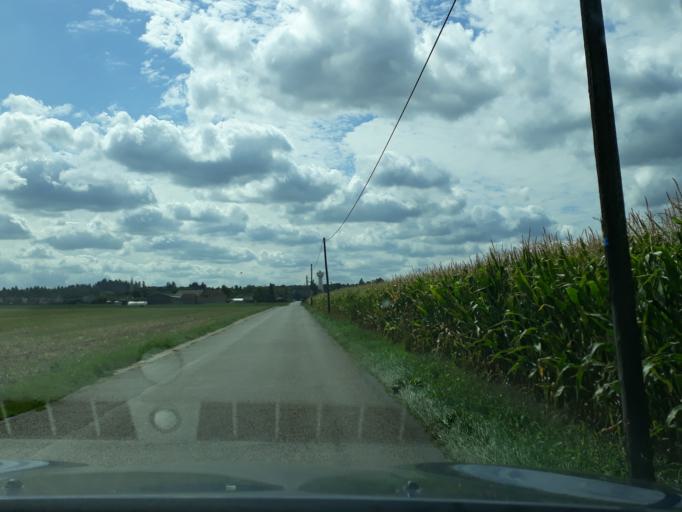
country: FR
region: Centre
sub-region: Departement du Loiret
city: Saint-Cyr-en-Val
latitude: 47.8418
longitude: 1.9709
